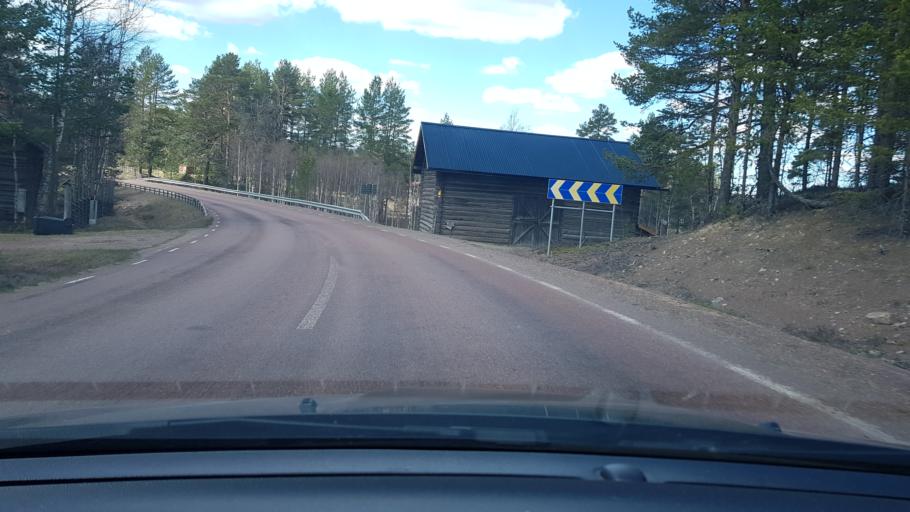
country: SE
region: Dalarna
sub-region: Alvdalens Kommun
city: AElvdalen
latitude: 61.0782
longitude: 13.6913
